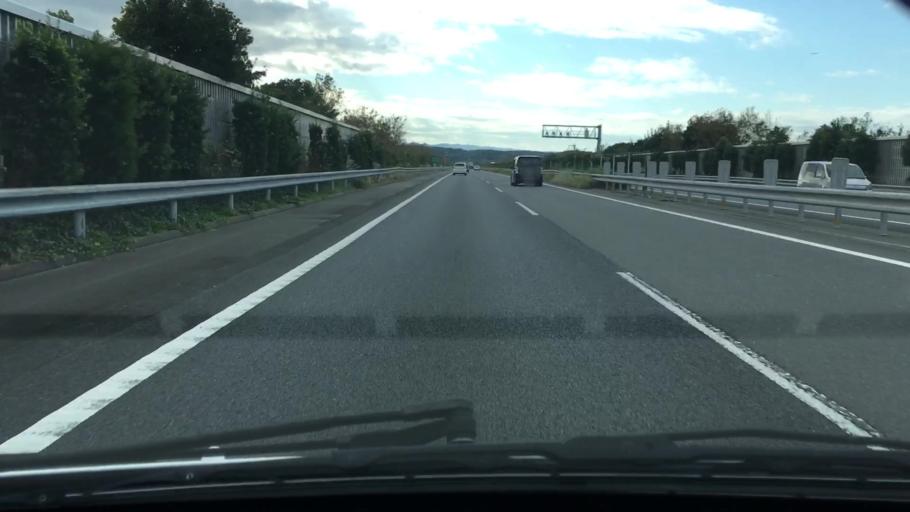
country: JP
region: Chiba
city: Kisarazu
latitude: 35.4131
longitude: 140.0106
